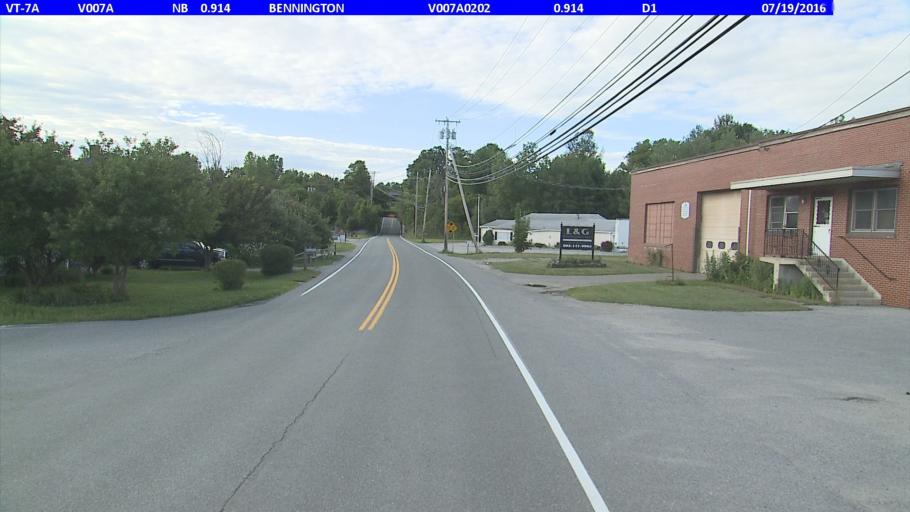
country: US
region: Vermont
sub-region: Bennington County
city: Bennington
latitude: 42.9028
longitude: -73.2120
